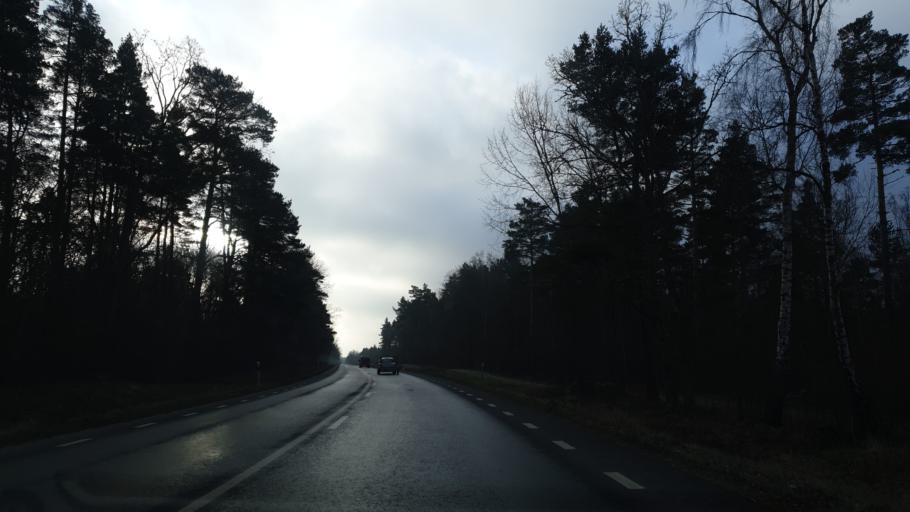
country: SE
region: Blekinge
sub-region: Karlshamns Kommun
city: Morrum
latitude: 56.1473
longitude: 14.6685
